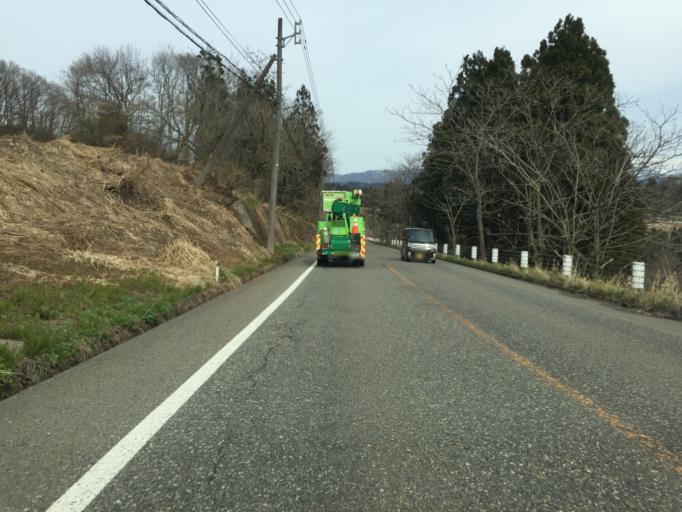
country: JP
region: Niigata
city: Tochio-honcho
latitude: 37.4524
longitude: 138.9604
